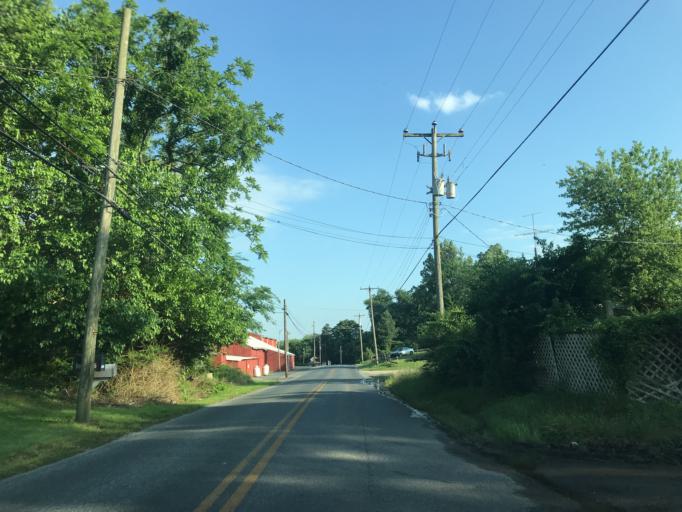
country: US
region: Maryland
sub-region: Caroline County
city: Federalsburg
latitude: 38.7038
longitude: -75.7762
